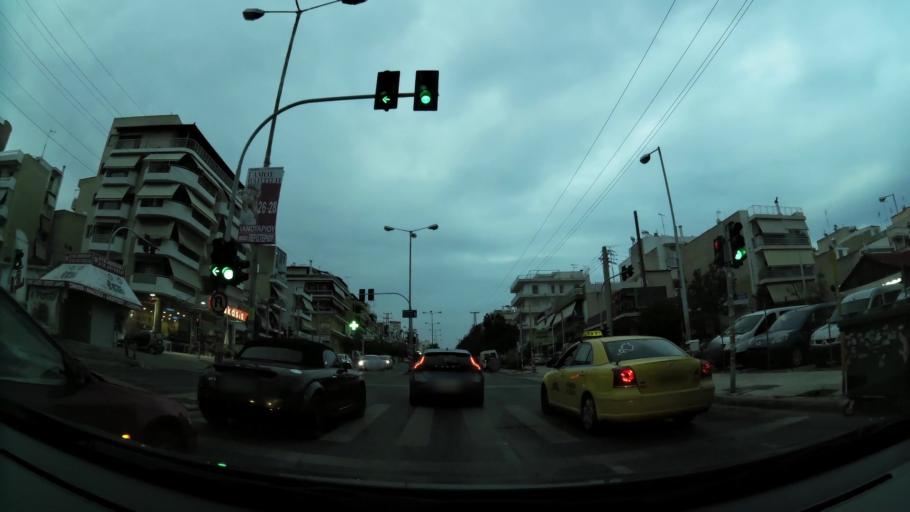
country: GR
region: Attica
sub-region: Nomos Piraios
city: Keratsini
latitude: 37.9679
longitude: 23.6178
